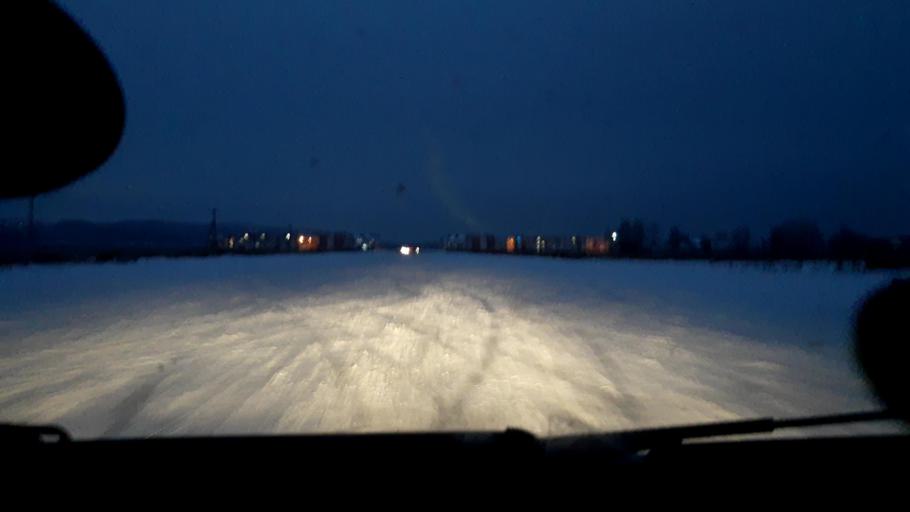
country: RU
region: Bashkortostan
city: Ufa
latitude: 54.8284
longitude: 56.1658
